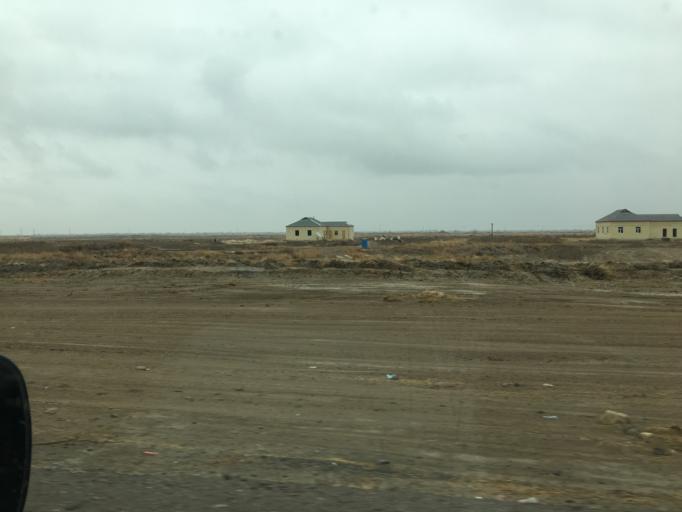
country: TM
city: Murgab
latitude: 37.4742
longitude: 62.0198
